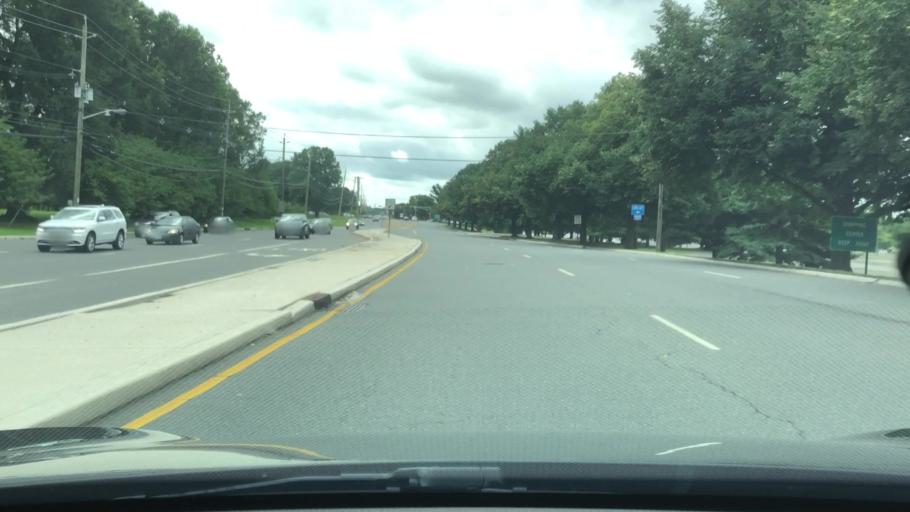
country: US
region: New Jersey
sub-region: Mercer County
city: Lawrenceville
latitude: 40.2933
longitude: -74.6782
